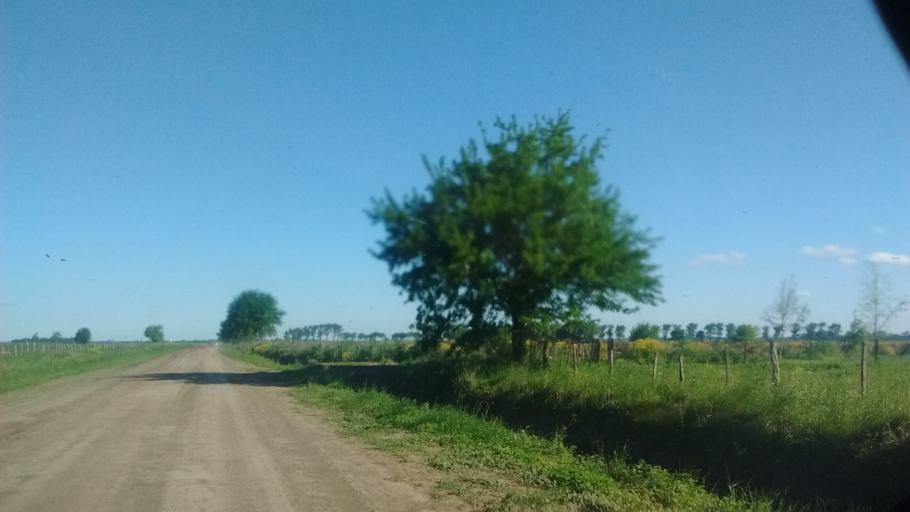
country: AR
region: Santa Fe
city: Funes
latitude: -32.8653
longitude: -60.8008
